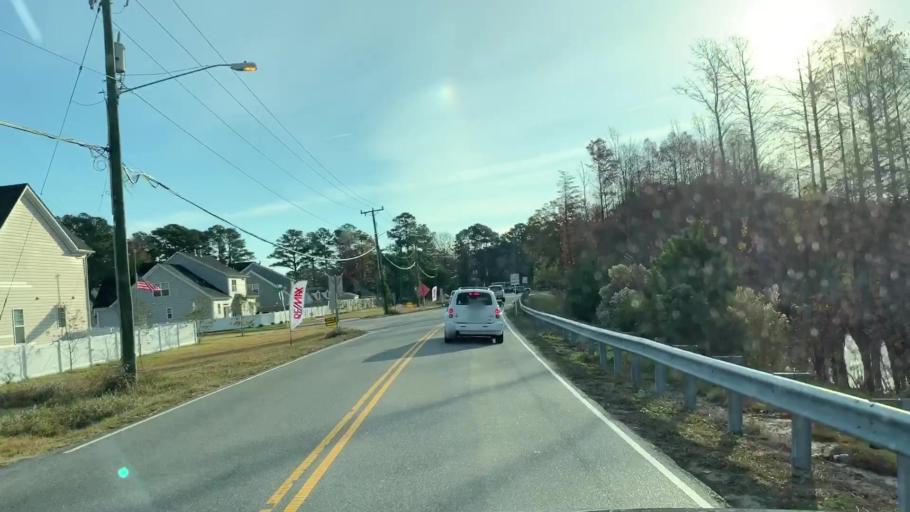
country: US
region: Virginia
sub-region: City of Chesapeake
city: Chesapeake
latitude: 36.7610
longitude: -76.1442
